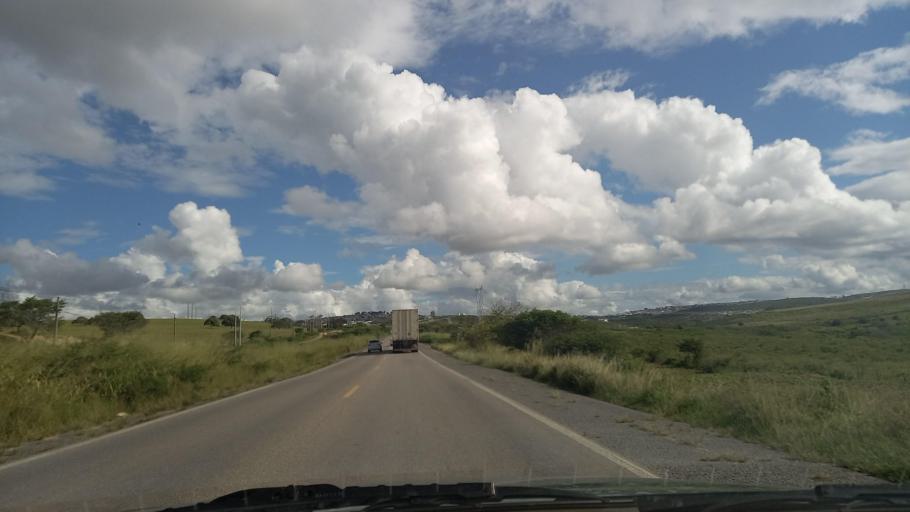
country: BR
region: Pernambuco
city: Garanhuns
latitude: -8.8452
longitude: -36.4595
